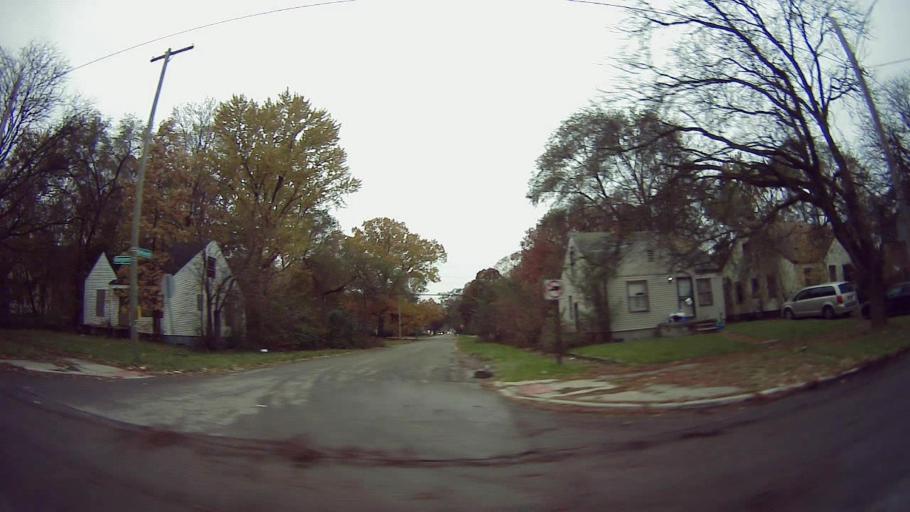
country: US
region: Michigan
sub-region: Wayne County
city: Dearborn Heights
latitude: 42.3741
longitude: -83.2364
